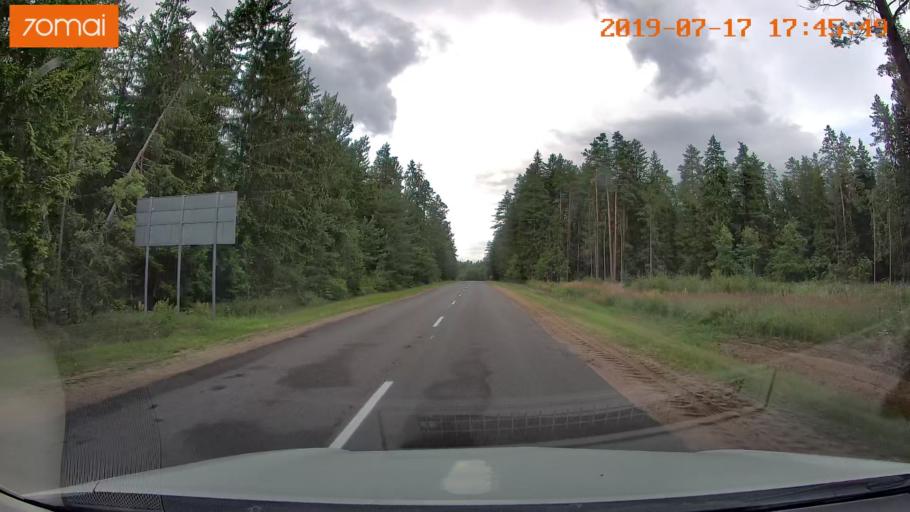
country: BY
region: Mogilev
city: Hlusha
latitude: 53.0909
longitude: 28.8459
